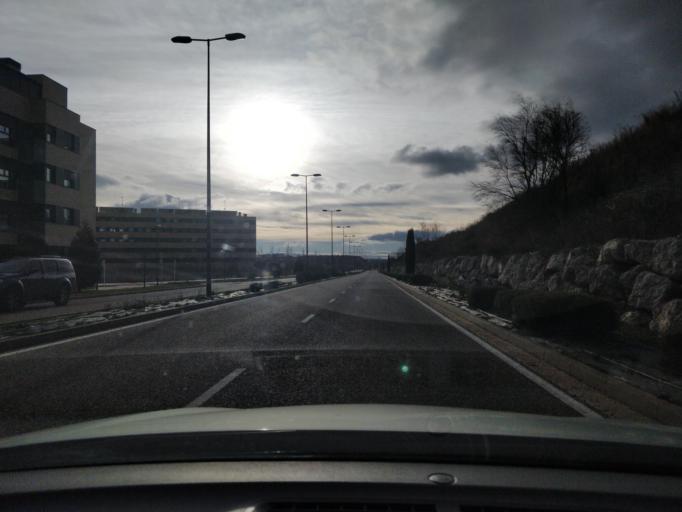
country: ES
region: Castille and Leon
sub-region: Provincia de Burgos
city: Burgos
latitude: 42.3496
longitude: -3.7182
